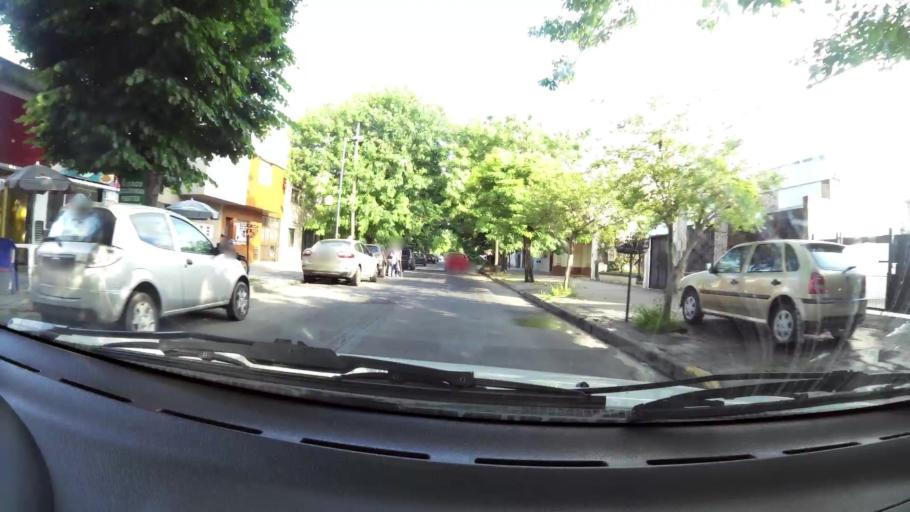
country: AR
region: Buenos Aires
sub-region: Partido de La Plata
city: La Plata
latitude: -34.8966
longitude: -57.9538
